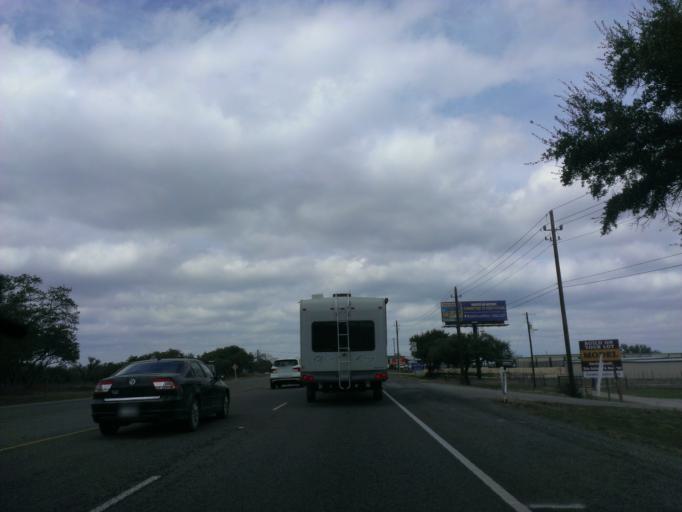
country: US
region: Texas
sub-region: Travis County
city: Briarcliff
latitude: 30.4596
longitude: -98.1566
